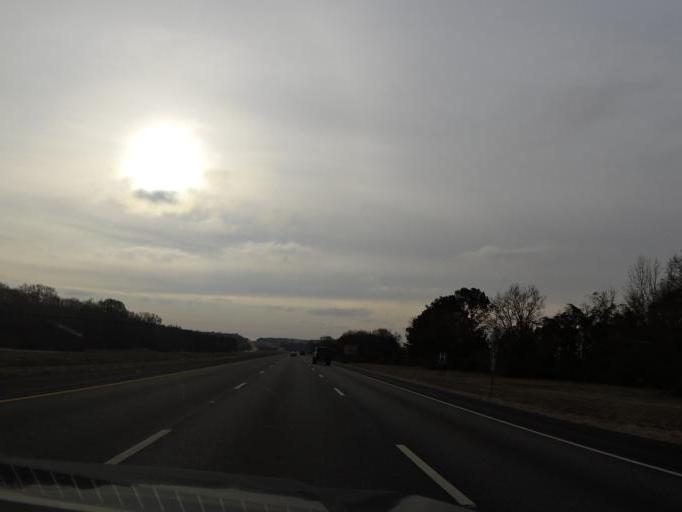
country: US
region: Alabama
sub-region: Autauga County
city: Prattville
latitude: 32.4979
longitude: -86.4161
